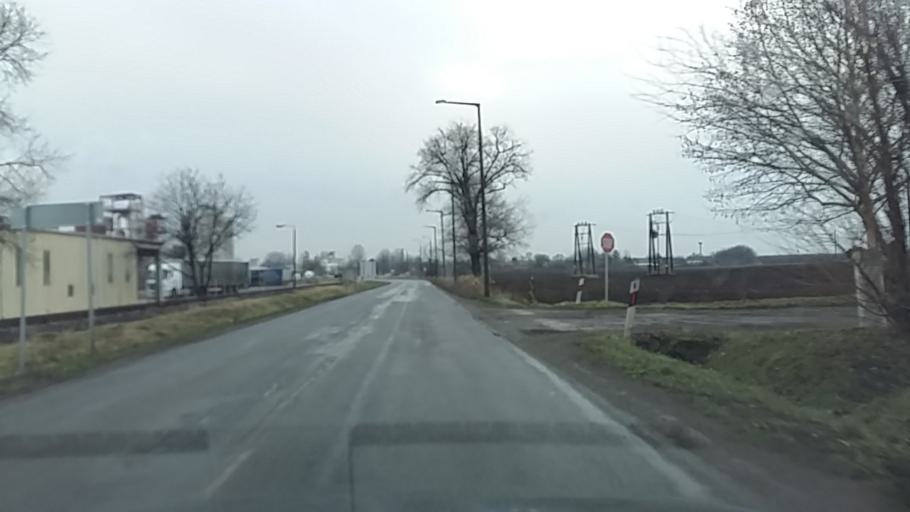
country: HU
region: Fejer
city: Pusztaszabolcs
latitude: 47.0835
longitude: 18.7126
